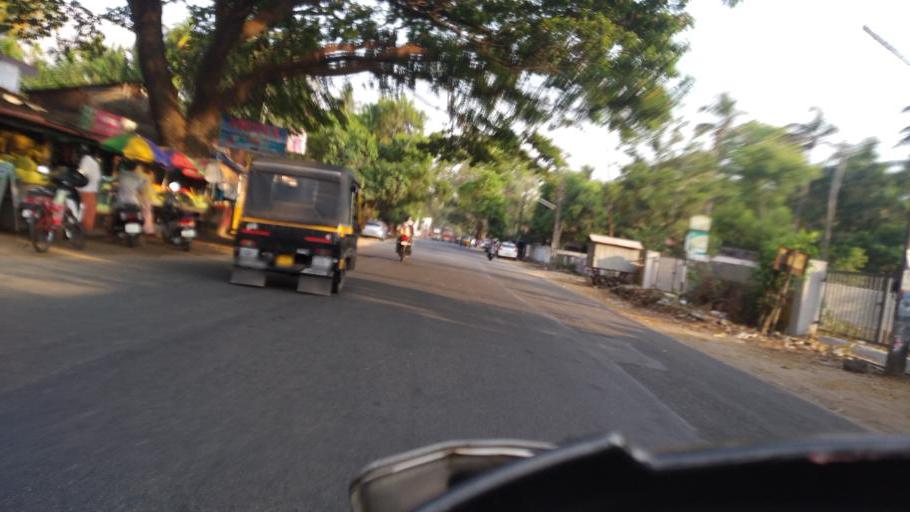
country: IN
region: Kerala
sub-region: Thrissur District
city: Thanniyam
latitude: 10.4097
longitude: 76.1093
